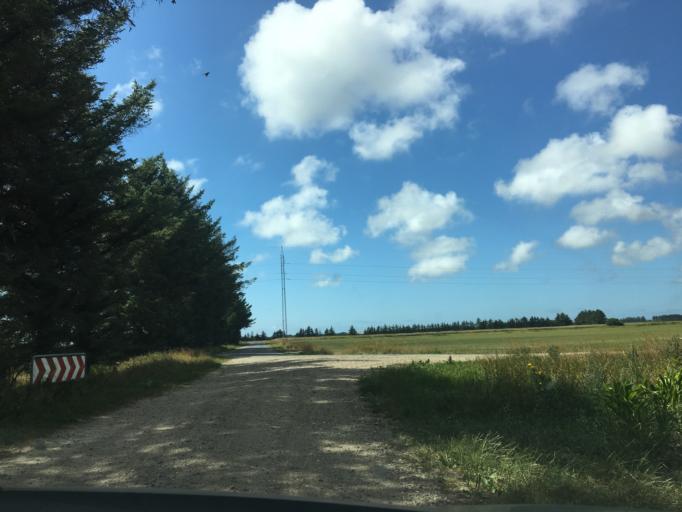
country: DK
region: South Denmark
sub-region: Varde Kommune
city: Oksbol
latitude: 55.8141
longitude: 8.2780
